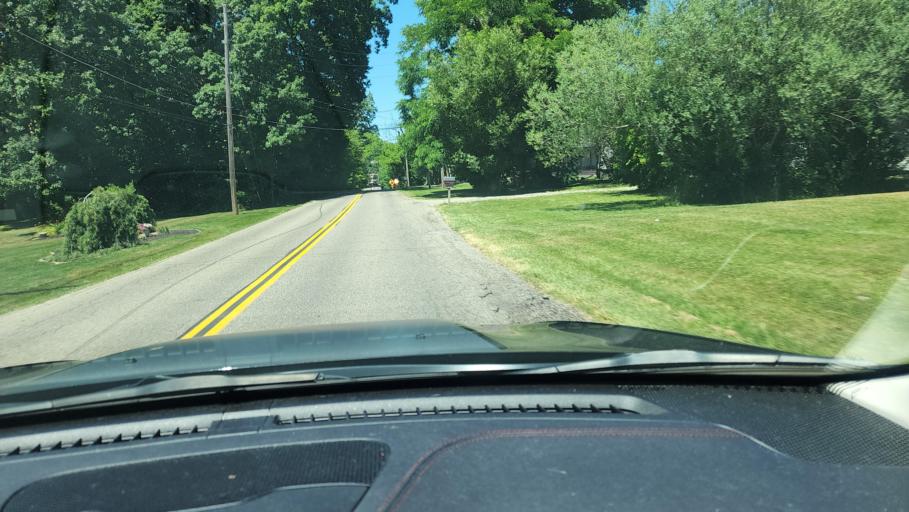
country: US
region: Ohio
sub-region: Mahoning County
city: Austintown
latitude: 41.0664
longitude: -80.7912
